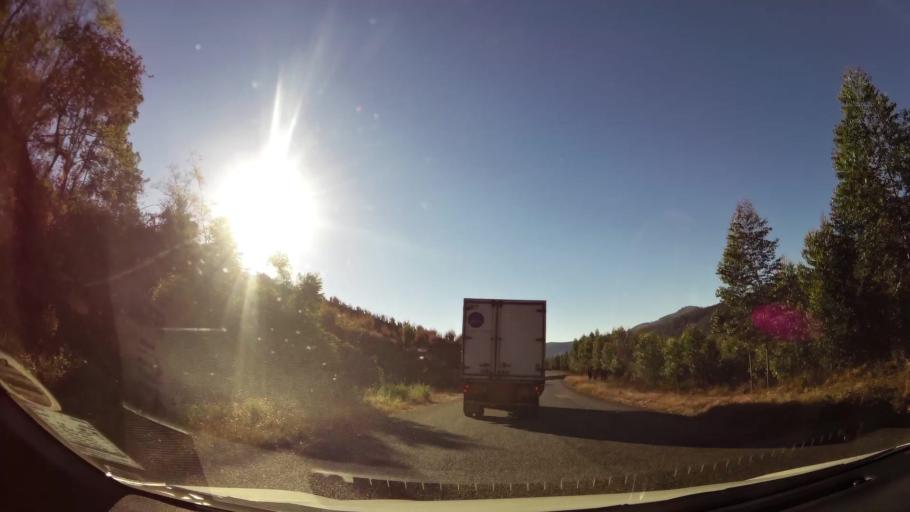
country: ZA
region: Limpopo
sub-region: Mopani District Municipality
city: Tzaneen
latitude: -23.9380
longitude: 30.0235
